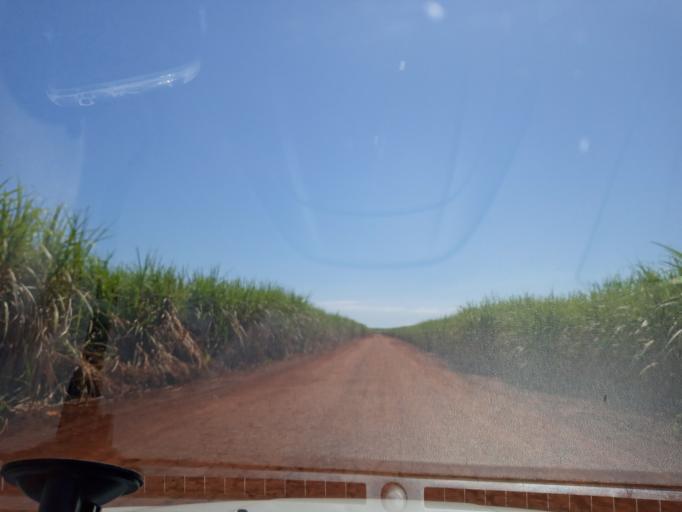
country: BR
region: Goias
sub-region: Itumbiara
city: Itumbiara
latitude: -18.4453
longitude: -49.1528
